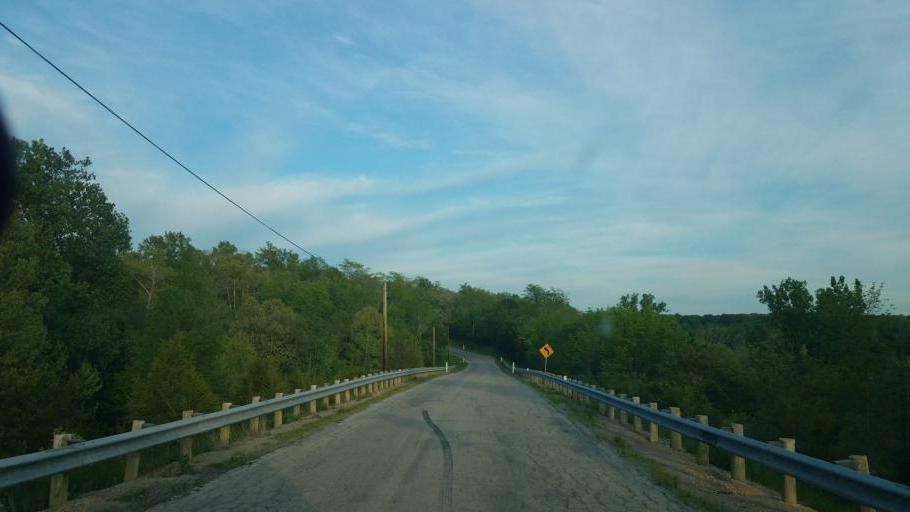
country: US
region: Ohio
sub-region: Highland County
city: Greenfield
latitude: 39.2789
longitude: -83.4164
